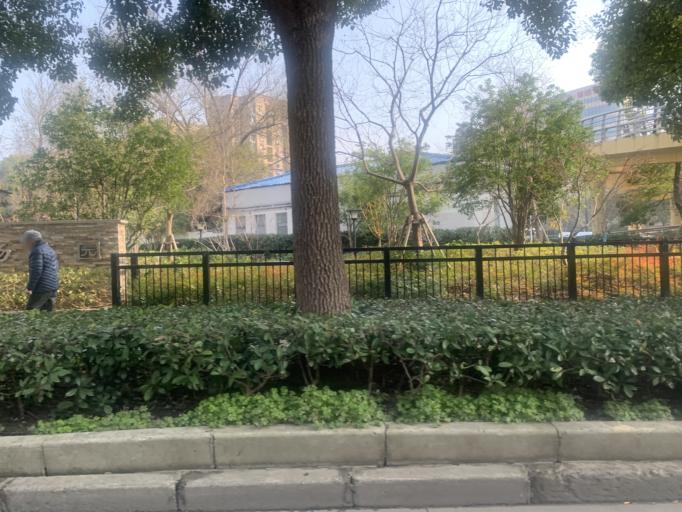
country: CN
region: Shanghai Shi
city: Huamu
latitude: 31.1823
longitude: 121.5158
